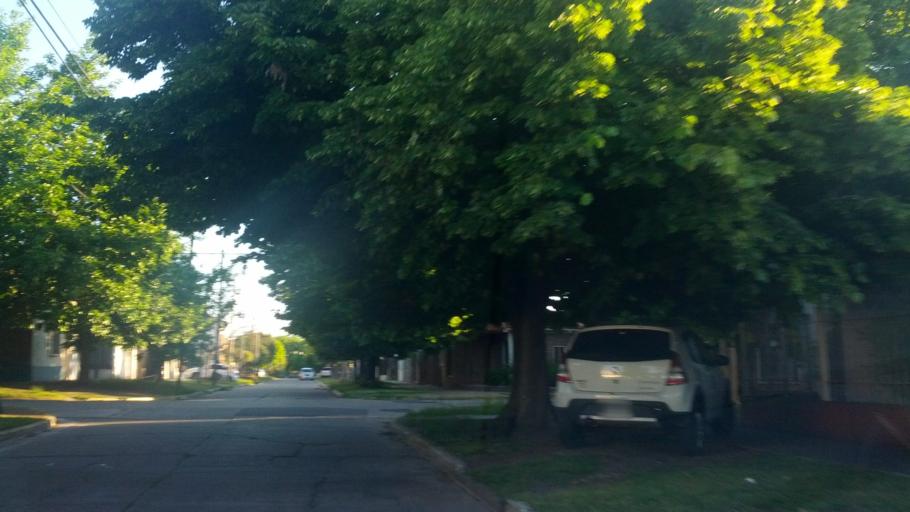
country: AR
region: Buenos Aires
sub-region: Partido de Lomas de Zamora
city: Lomas de Zamora
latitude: -34.7681
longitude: -58.4147
